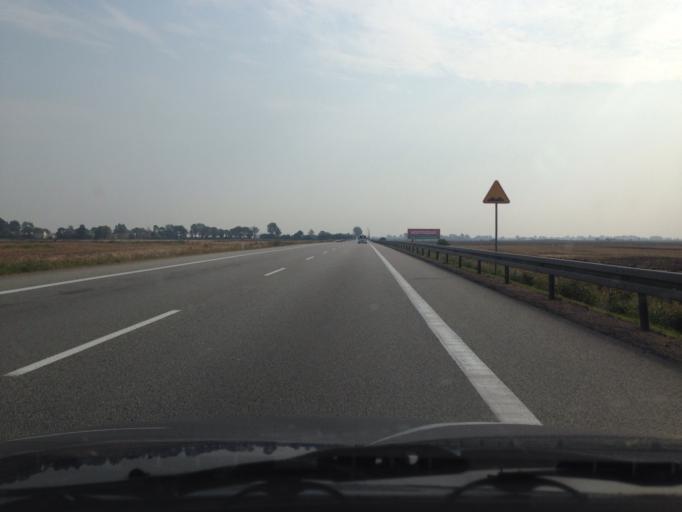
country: PL
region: Pomeranian Voivodeship
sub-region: Powiat nowodworski
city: Ostaszewo
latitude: 54.2413
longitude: 19.0115
